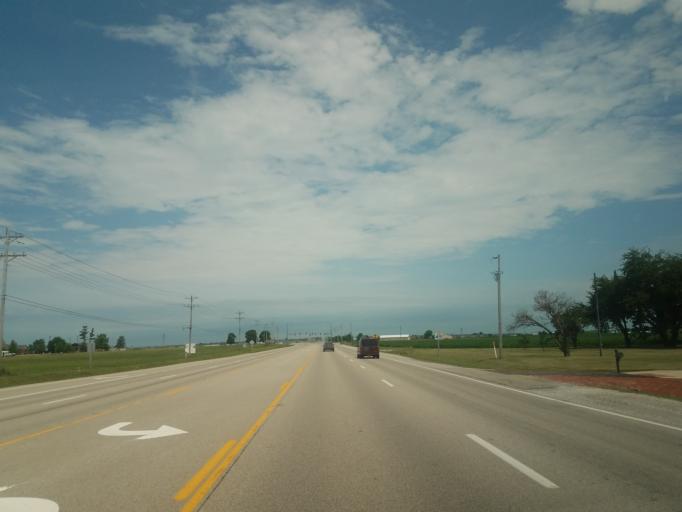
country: US
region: Illinois
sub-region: McLean County
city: Downs
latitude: 40.4697
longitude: -88.9021
